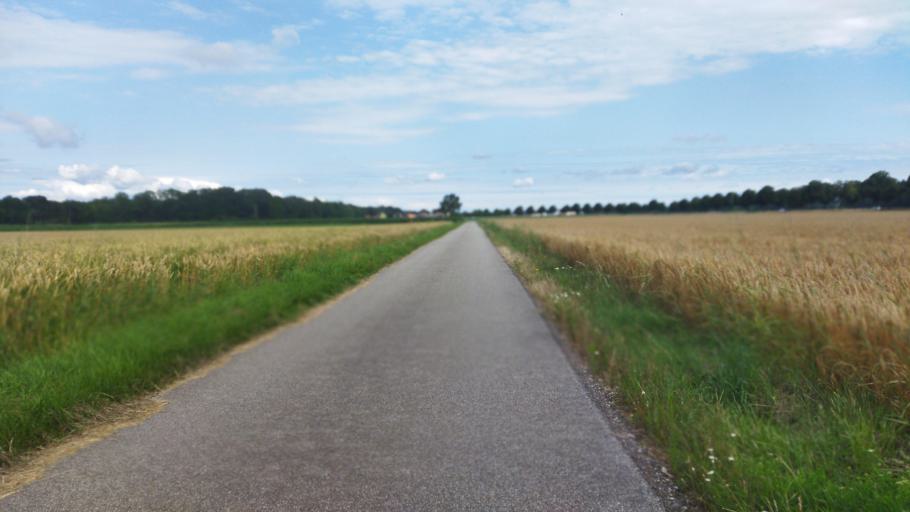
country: DE
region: Bavaria
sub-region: Upper Palatinate
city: Mintraching
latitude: 48.9861
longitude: 12.2570
